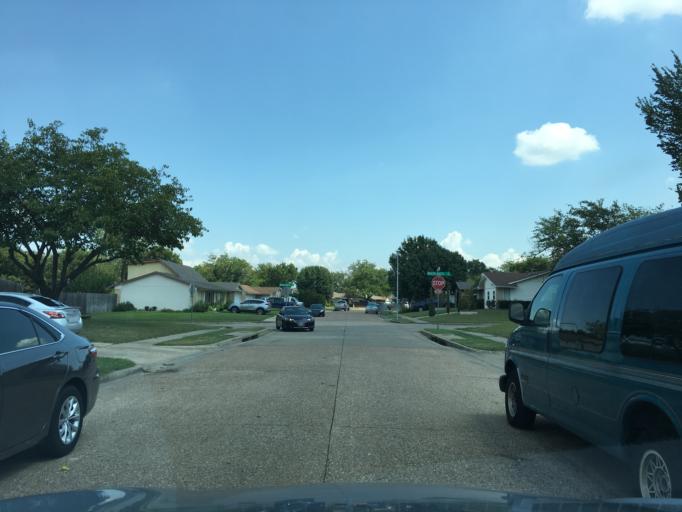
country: US
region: Texas
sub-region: Dallas County
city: Garland
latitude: 32.9397
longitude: -96.6527
